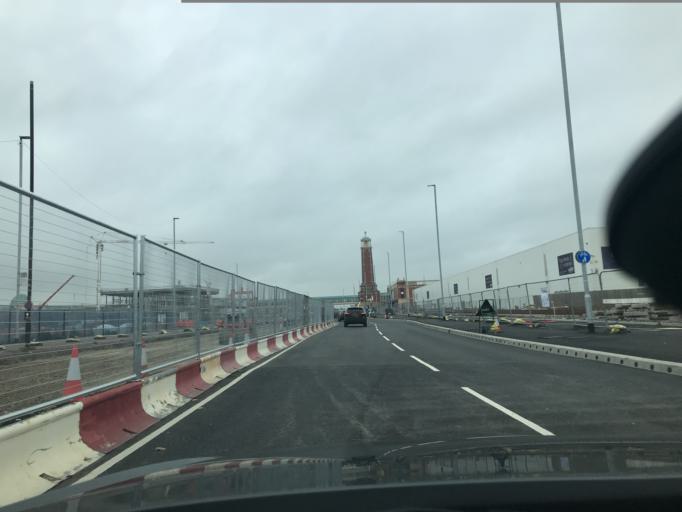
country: GB
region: England
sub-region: City and Borough of Salford
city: Eccles
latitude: 53.4637
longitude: -2.3374
